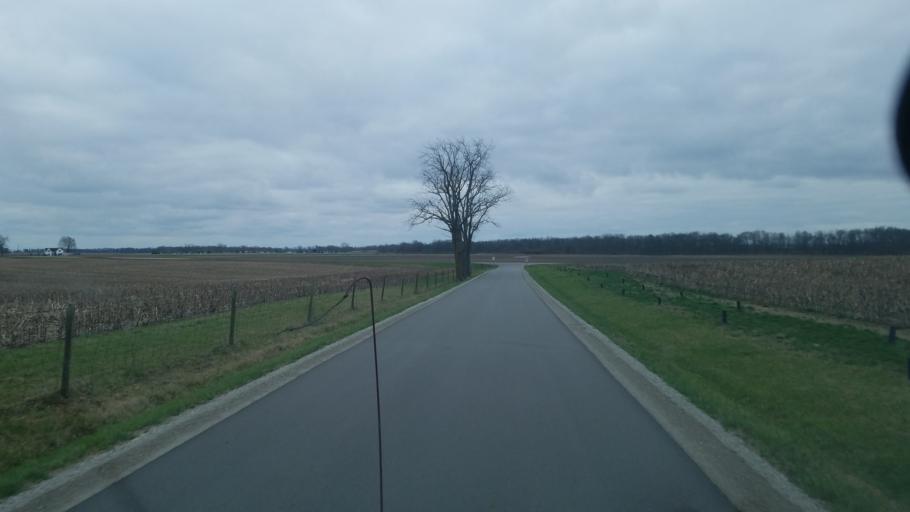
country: US
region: Ohio
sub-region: Fayette County
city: Jeffersonville
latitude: 39.5847
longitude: -83.5174
